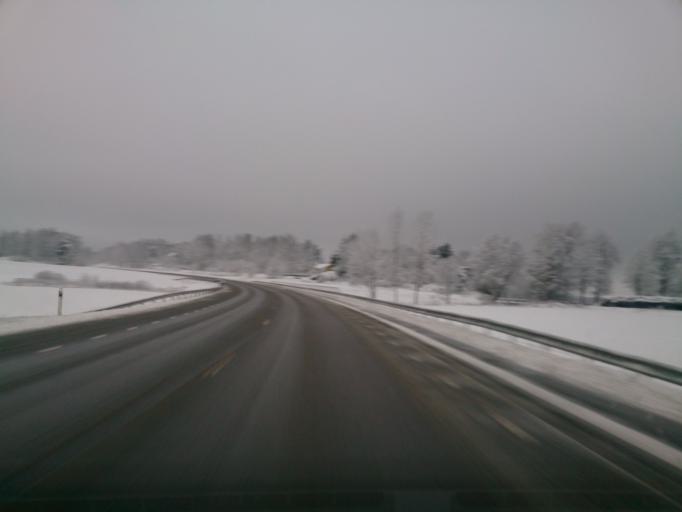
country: SE
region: OEstergoetland
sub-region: Atvidabergs Kommun
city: Atvidaberg
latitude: 58.2336
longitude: 15.9606
